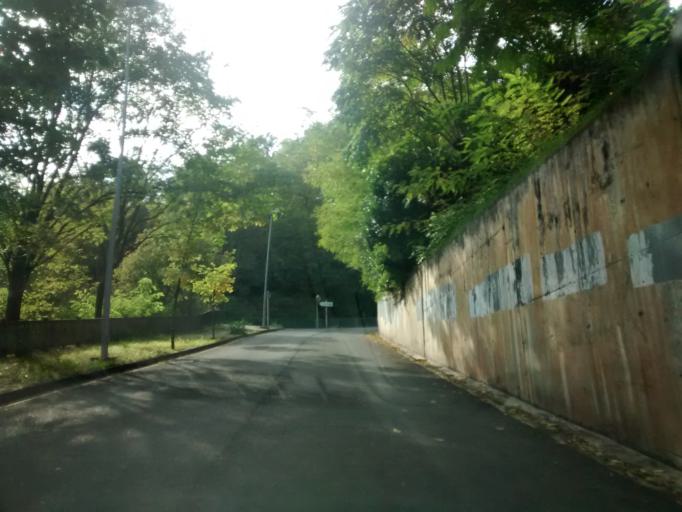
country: ES
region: Basque Country
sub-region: Provincia de Guipuzcoa
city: Eibar
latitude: 43.1920
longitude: -2.4520
